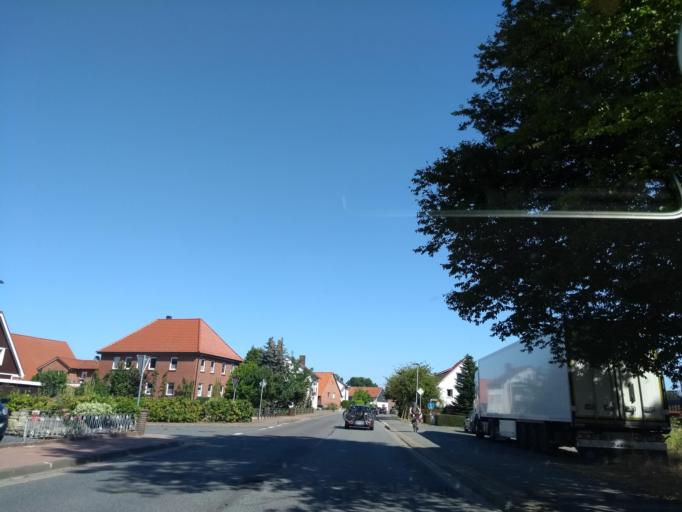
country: DE
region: Lower Saxony
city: Bad Nenndorf
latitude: 52.3558
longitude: 9.3874
